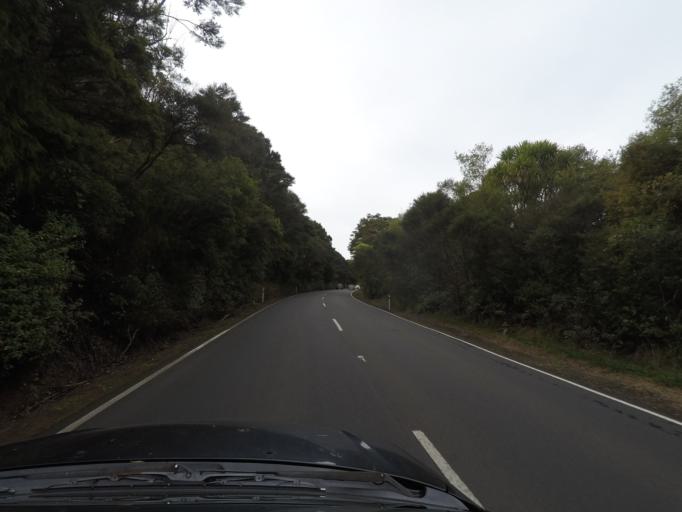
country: NZ
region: Auckland
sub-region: Auckland
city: Titirangi
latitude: -36.9332
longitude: 174.5676
